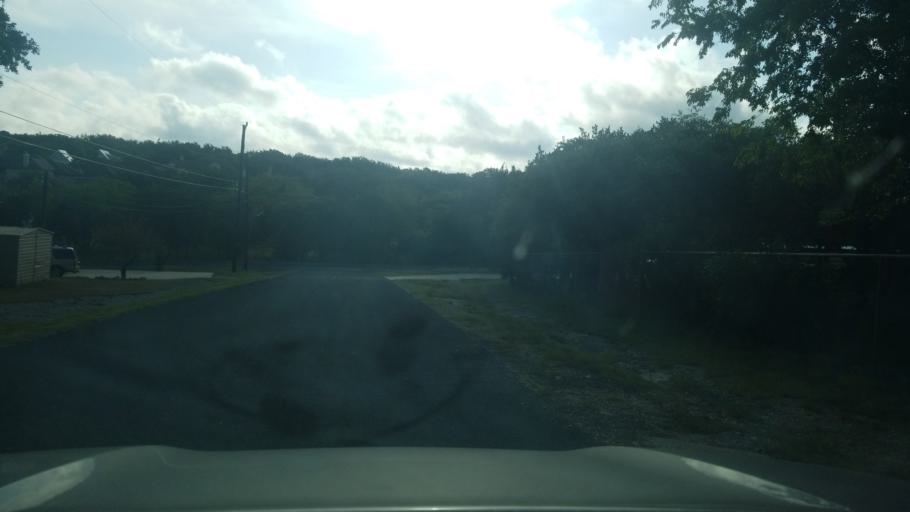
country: US
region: Texas
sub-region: Bexar County
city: Timberwood Park
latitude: 29.7012
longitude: -98.5130
